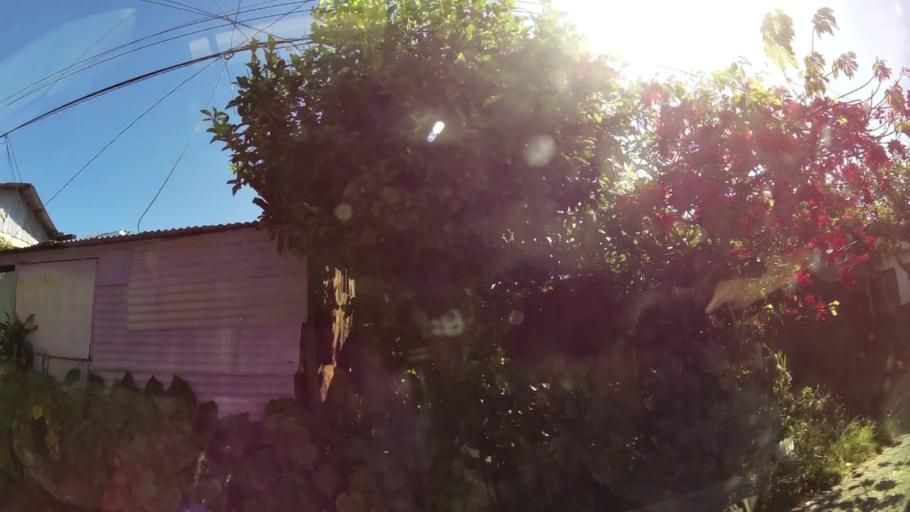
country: SV
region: Sonsonate
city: Juayua
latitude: 13.8445
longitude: -89.7438
